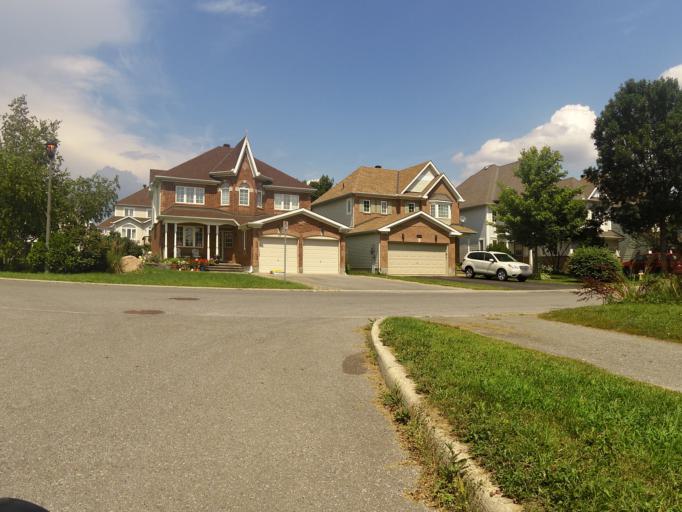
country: CA
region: Ontario
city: Bells Corners
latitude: 45.3117
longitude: -75.9297
